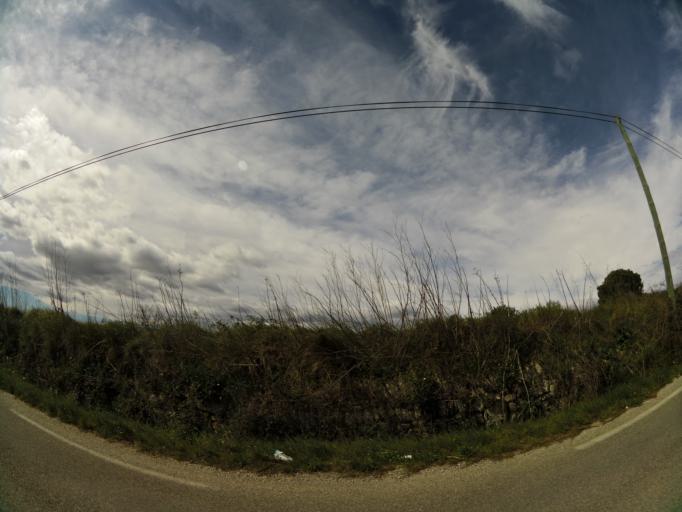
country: FR
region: Languedoc-Roussillon
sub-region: Departement du Gard
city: Gallargues-le-Montueux
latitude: 43.7104
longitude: 4.1707
